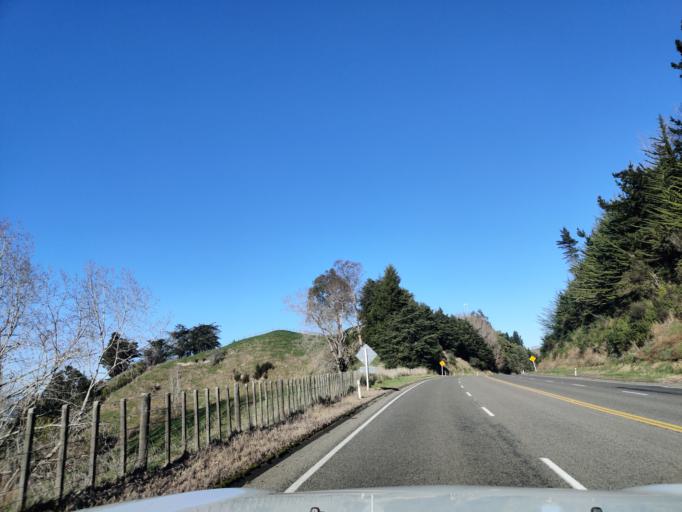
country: NZ
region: Manawatu-Wanganui
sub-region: Ruapehu District
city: Waiouru
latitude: -39.7689
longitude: 175.7992
